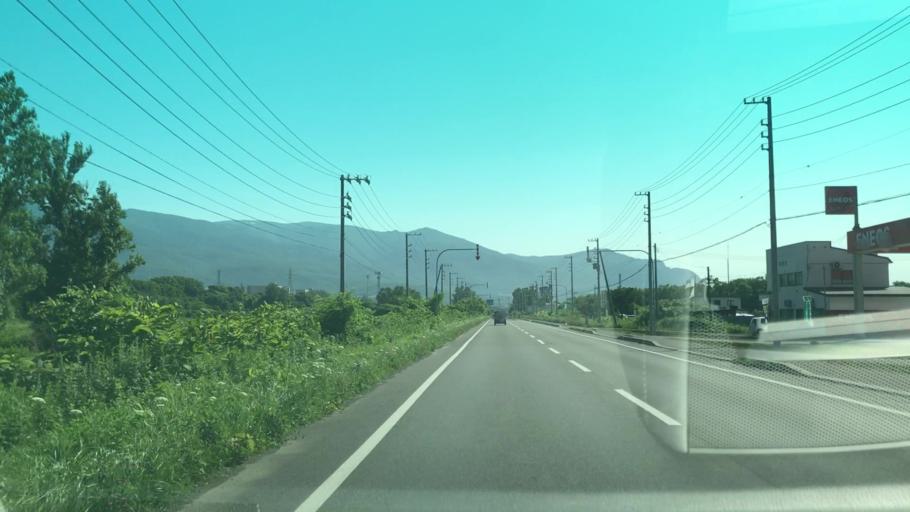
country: JP
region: Hokkaido
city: Iwanai
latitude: 42.9957
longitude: 140.5358
